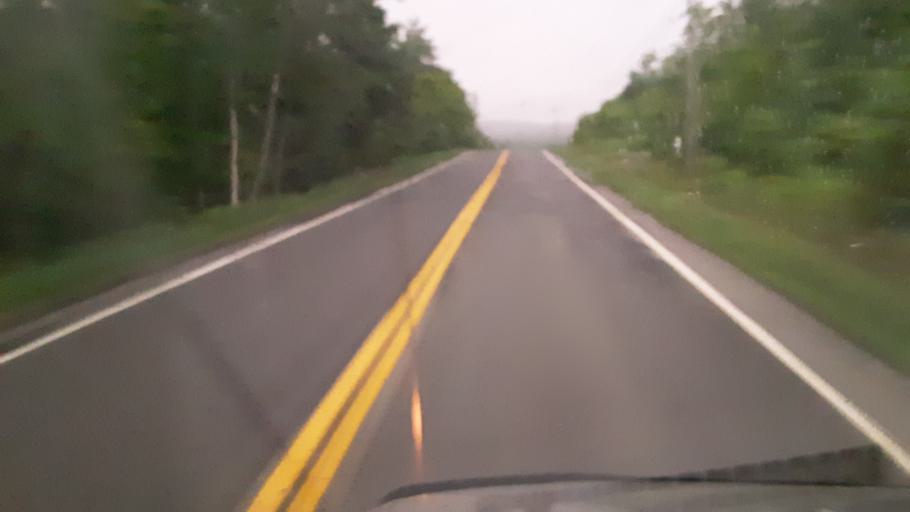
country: US
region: Maine
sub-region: Penobscot County
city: Patten
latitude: 46.1126
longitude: -68.4105
